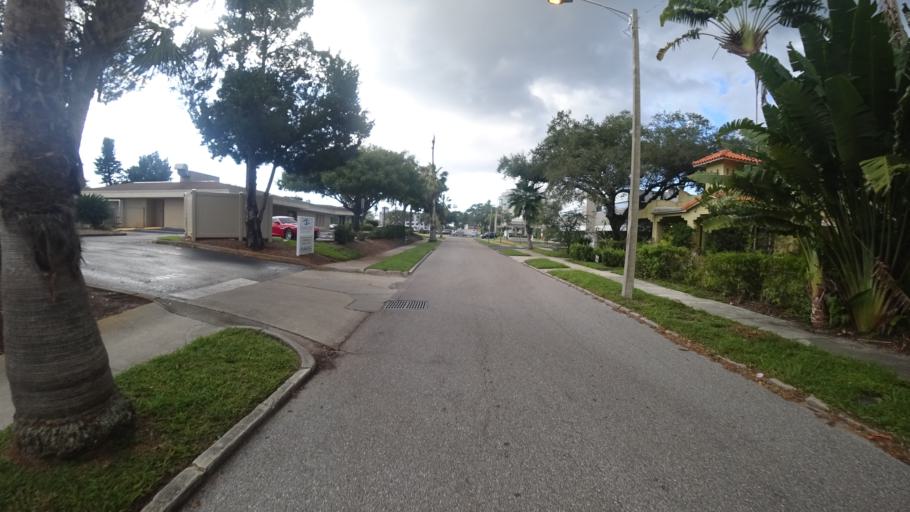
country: US
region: Florida
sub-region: Manatee County
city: Bradenton
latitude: 27.4959
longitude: -82.5603
